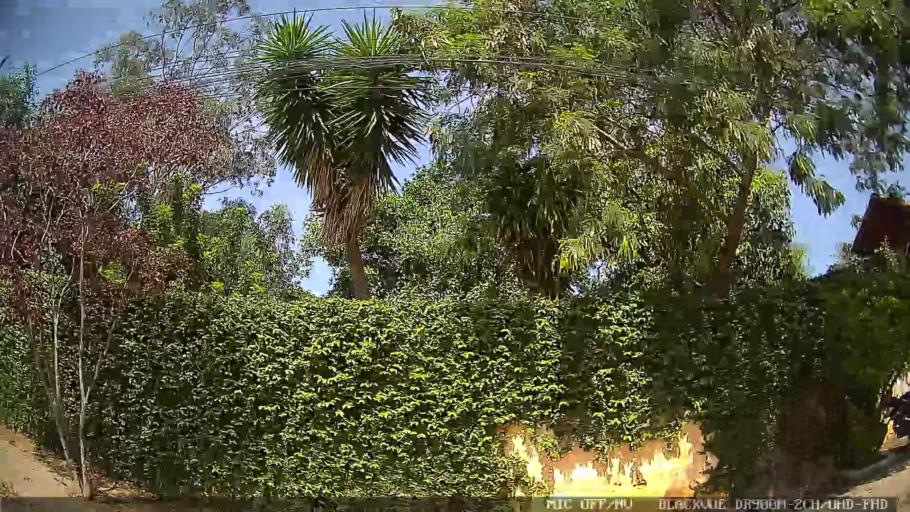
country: BR
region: Sao Paulo
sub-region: Cabreuva
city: Cabreuva
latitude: -23.2751
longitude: -47.0564
